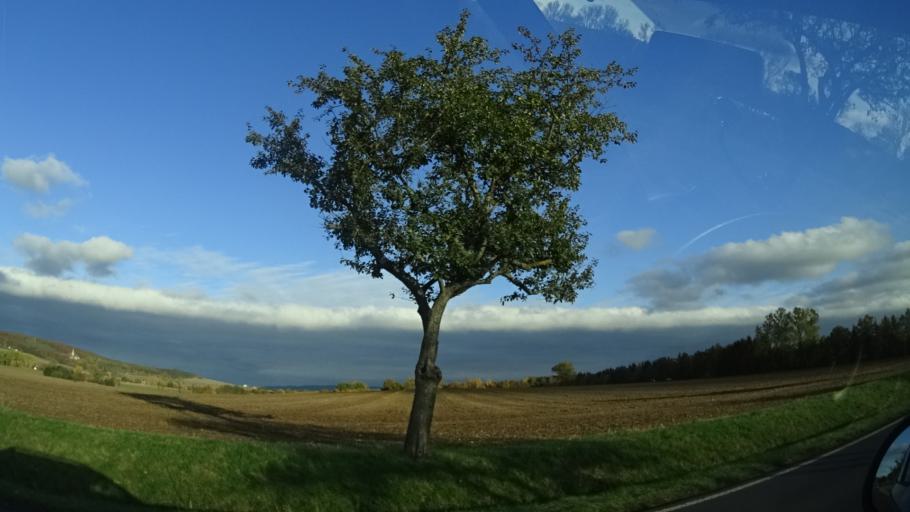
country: DE
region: Thuringia
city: Nauendorf
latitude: 50.8810
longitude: 11.1854
